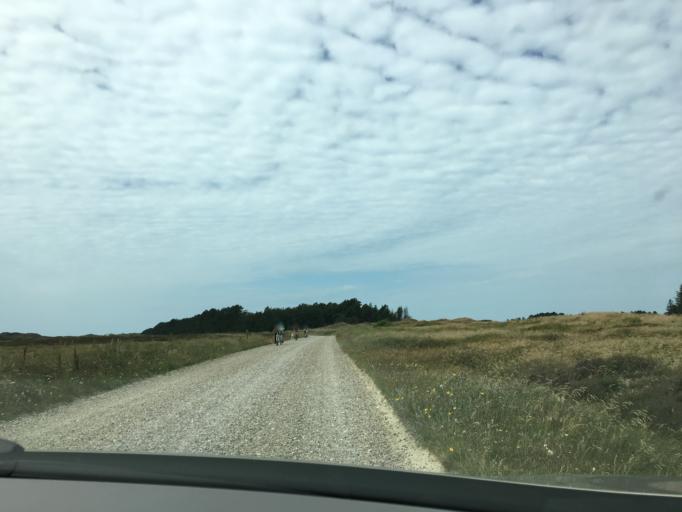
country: DK
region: South Denmark
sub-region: Varde Kommune
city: Oksbol
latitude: 55.7233
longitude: 8.2016
